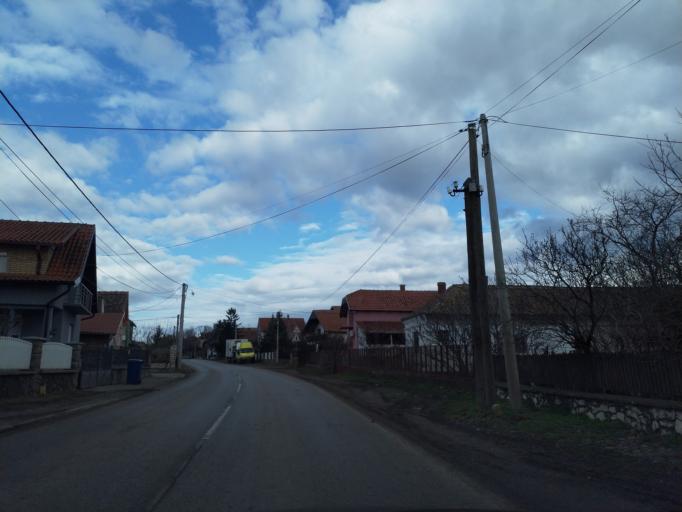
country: RS
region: Central Serbia
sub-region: Belgrade
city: Grocka
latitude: 44.6063
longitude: 20.7254
